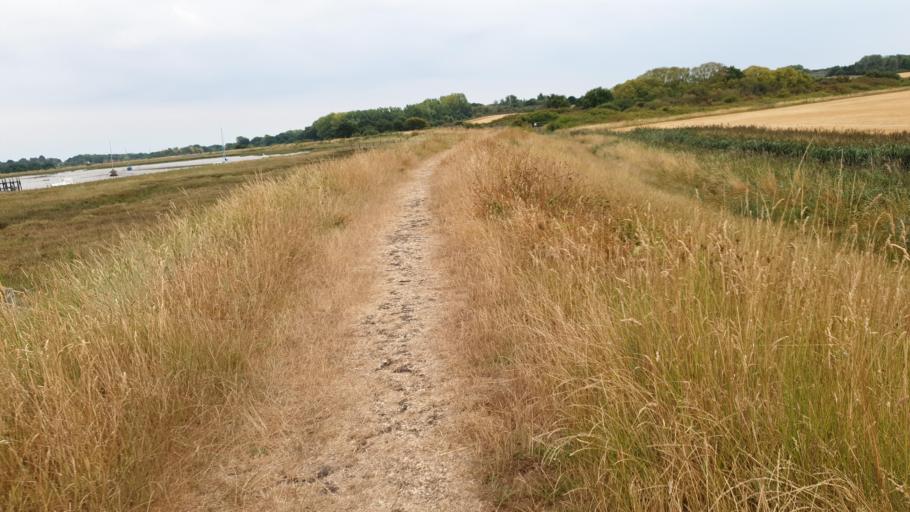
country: GB
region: England
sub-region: Essex
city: Alresford
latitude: 51.8366
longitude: 0.9917
